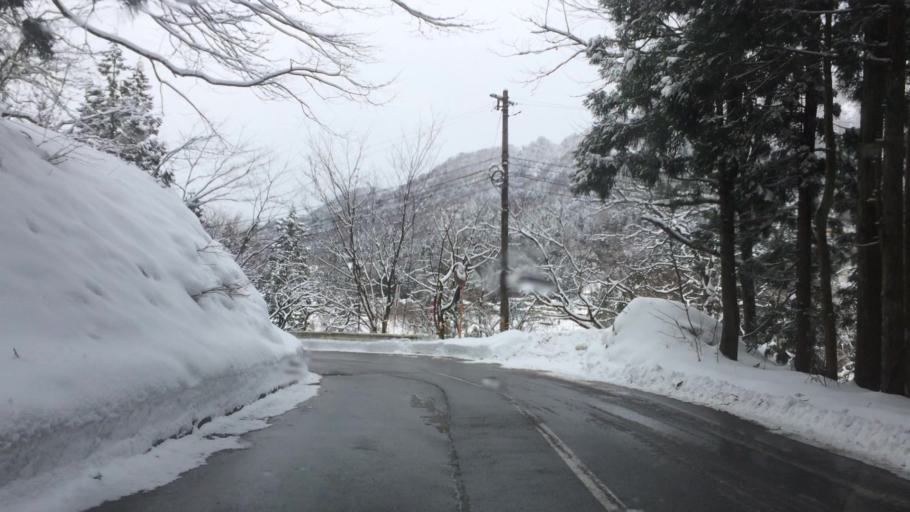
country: JP
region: Toyama
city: Kamiichi
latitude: 36.5715
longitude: 137.3732
